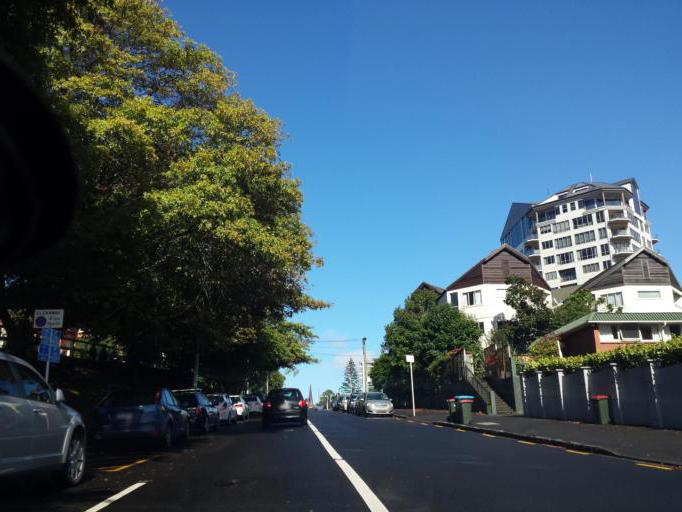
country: NZ
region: Auckland
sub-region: Auckland
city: Auckland
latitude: -36.8609
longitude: 174.7665
